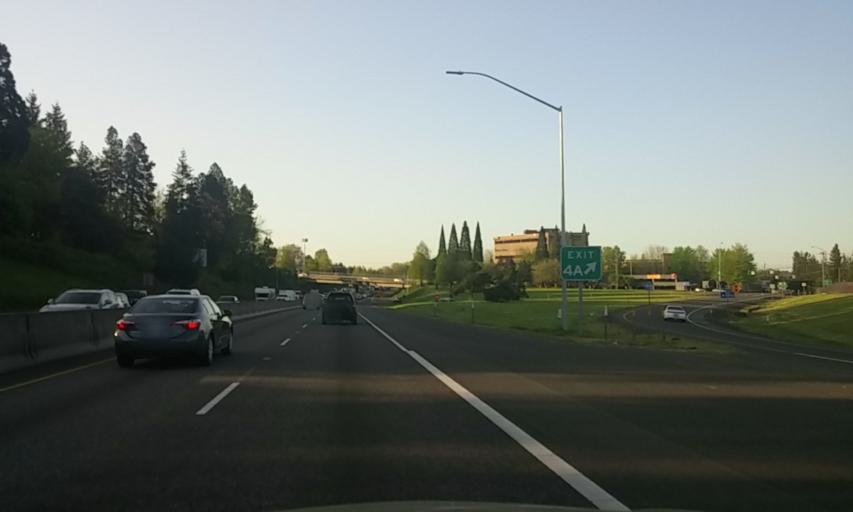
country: US
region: Oregon
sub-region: Washington County
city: Garden Home-Whitford
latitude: 45.4608
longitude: -122.7856
